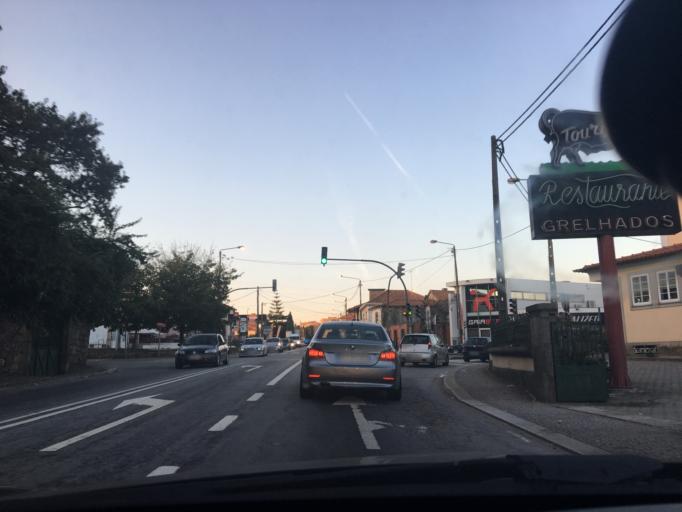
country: PT
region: Porto
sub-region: Maia
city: Gemunde
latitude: 41.2451
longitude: -8.6485
